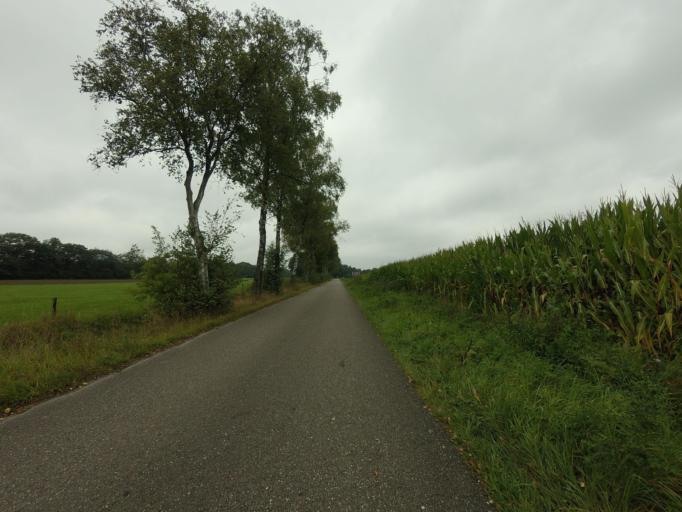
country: NL
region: Overijssel
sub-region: Gemeente Enschede
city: Enschede
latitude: 52.1859
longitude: 6.9335
